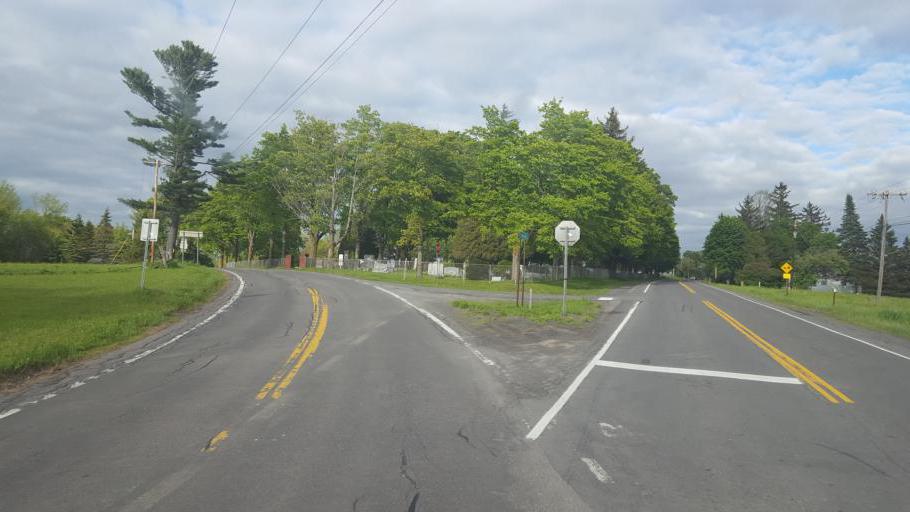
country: US
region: New York
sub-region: Otsego County
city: Richfield Springs
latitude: 42.9152
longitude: -74.9413
